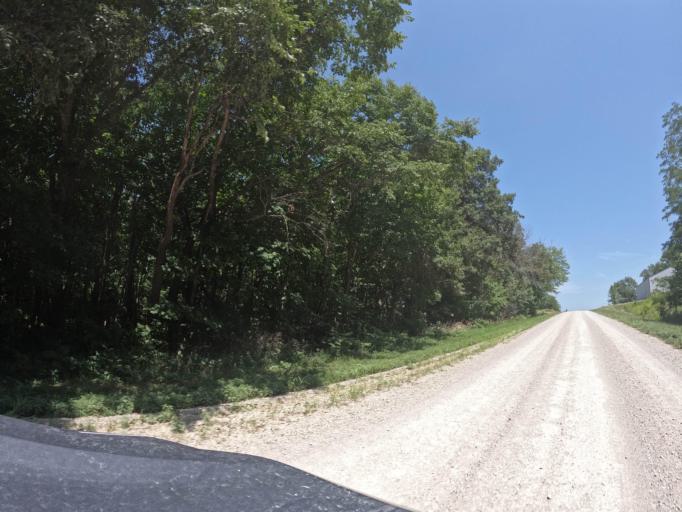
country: US
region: Iowa
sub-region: Henry County
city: Mount Pleasant
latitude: 40.9450
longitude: -91.6744
